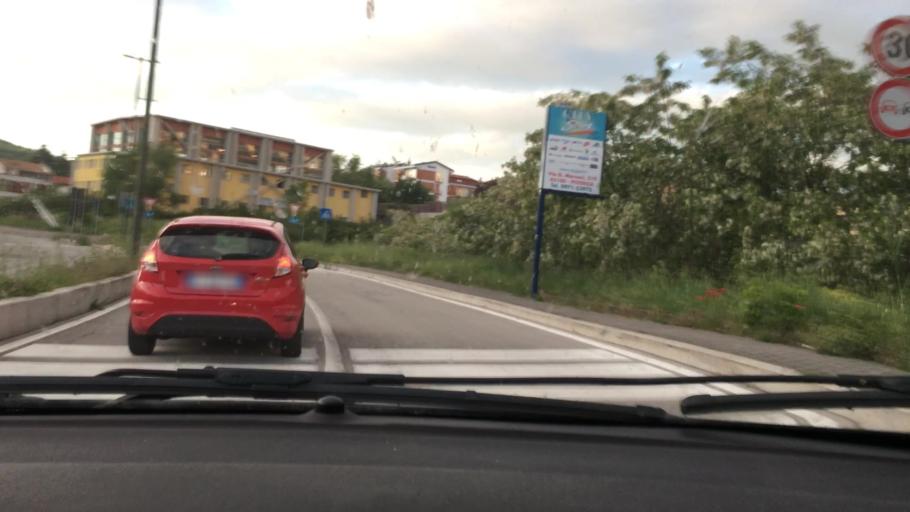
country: IT
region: Basilicate
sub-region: Provincia di Potenza
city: Potenza
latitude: 40.6419
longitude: 15.7998
